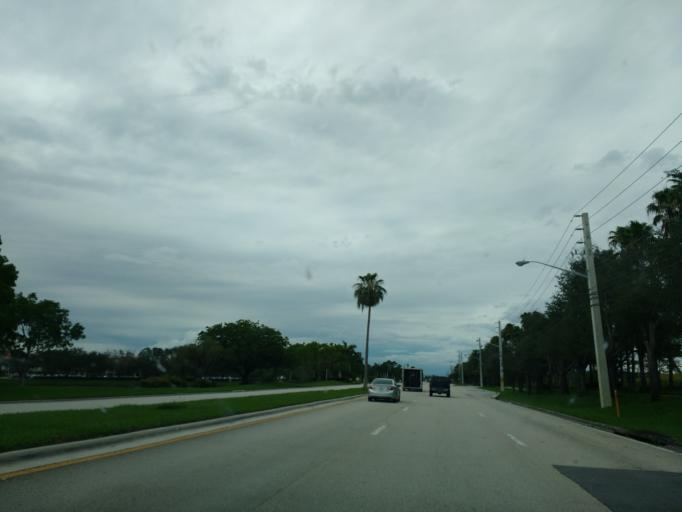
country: US
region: Florida
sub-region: Broward County
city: Pine Island Ridge
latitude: 26.1406
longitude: -80.3300
